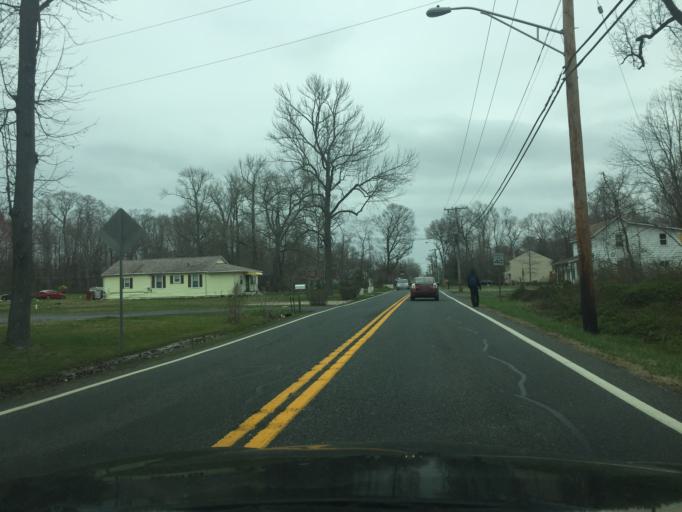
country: US
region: Maryland
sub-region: Baltimore County
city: Bowleys Quarters
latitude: 39.3519
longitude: -76.3775
